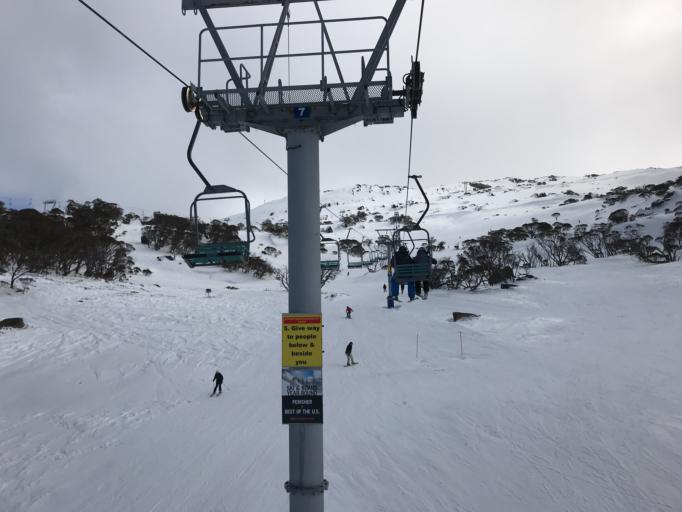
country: AU
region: New South Wales
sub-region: Snowy River
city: Jindabyne
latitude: -36.3998
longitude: 148.4009
